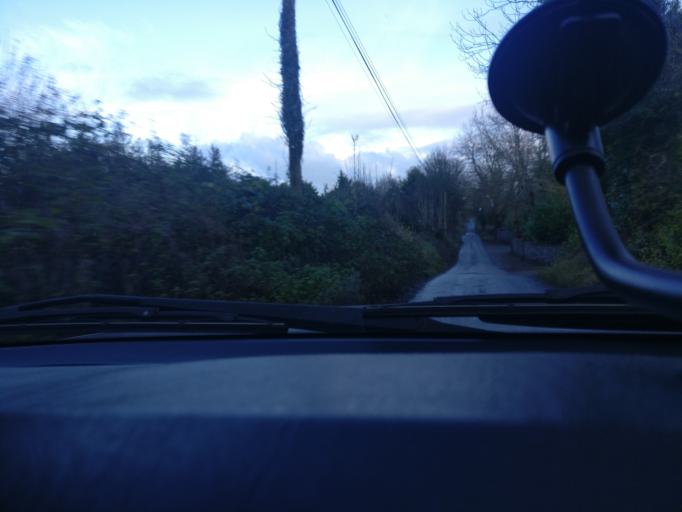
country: IE
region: Connaught
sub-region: County Galway
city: Athenry
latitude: 53.1991
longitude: -8.7076
